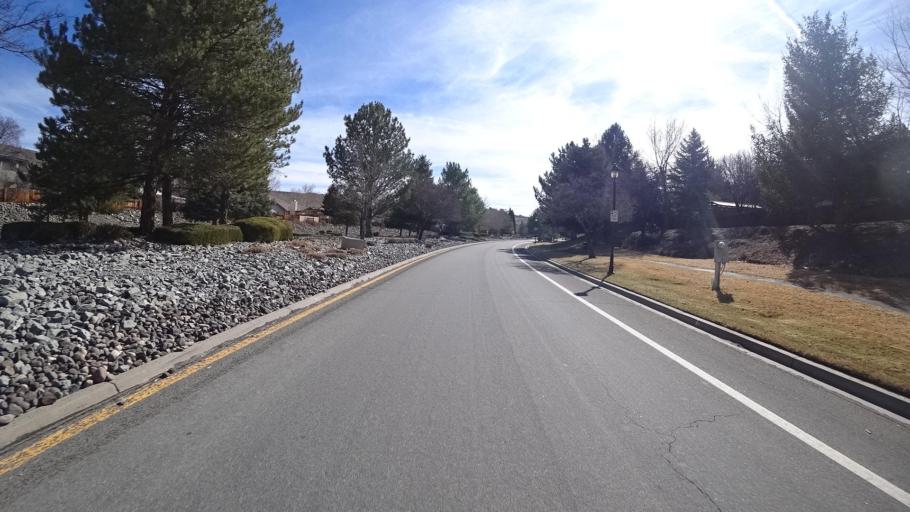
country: US
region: Nevada
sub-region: Washoe County
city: Spanish Springs
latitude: 39.5856
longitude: -119.7107
